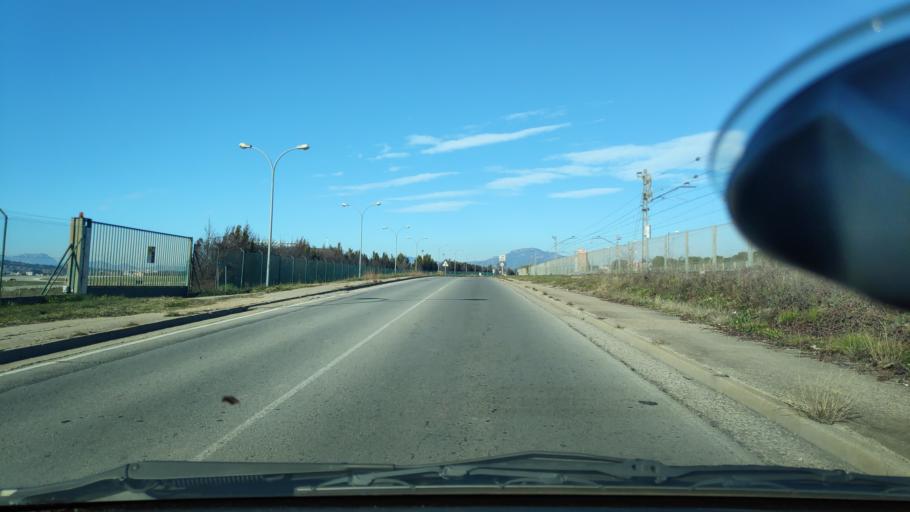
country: ES
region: Catalonia
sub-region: Provincia de Barcelona
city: Barbera del Valles
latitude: 41.5190
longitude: 2.1113
